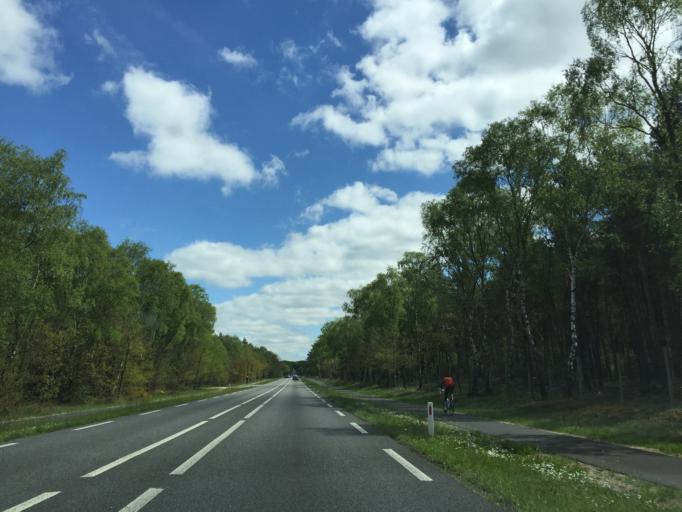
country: NL
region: Gelderland
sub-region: Gemeente Apeldoorn
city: Uddel
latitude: 52.2218
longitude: 5.7980
